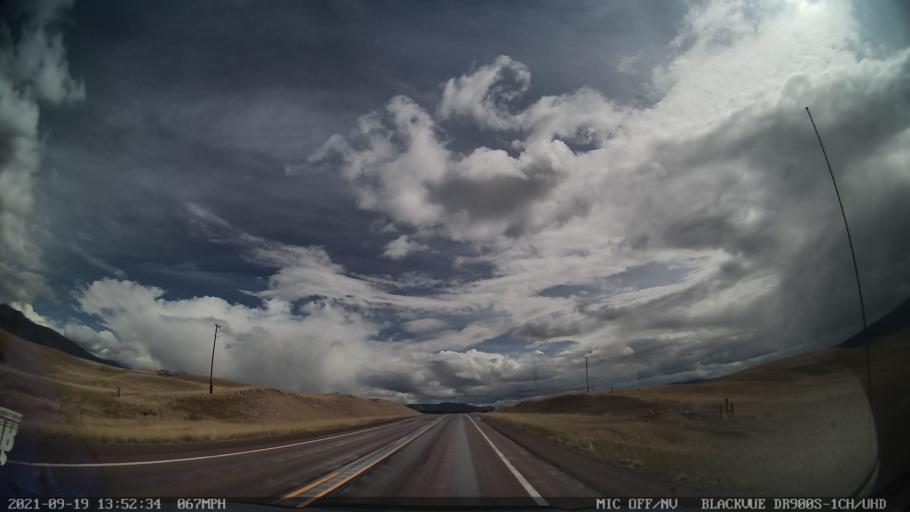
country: US
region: Montana
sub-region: Missoula County
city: Seeley Lake
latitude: 47.0353
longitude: -113.1528
